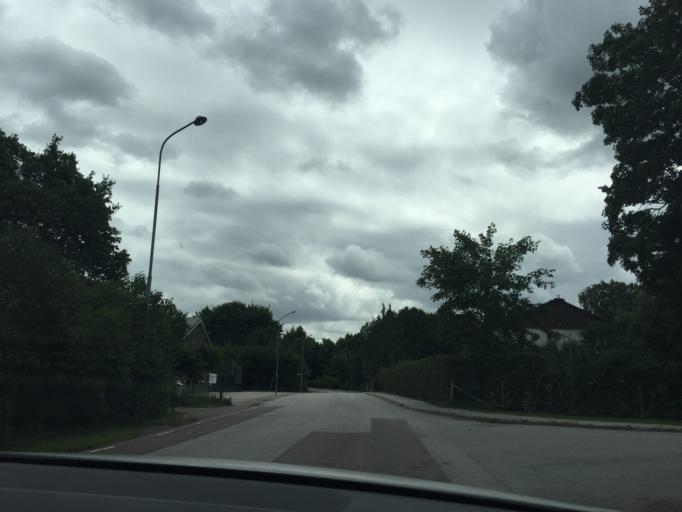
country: SE
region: Skane
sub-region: Sjobo Kommun
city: Blentarp
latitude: 55.5869
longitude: 13.6003
